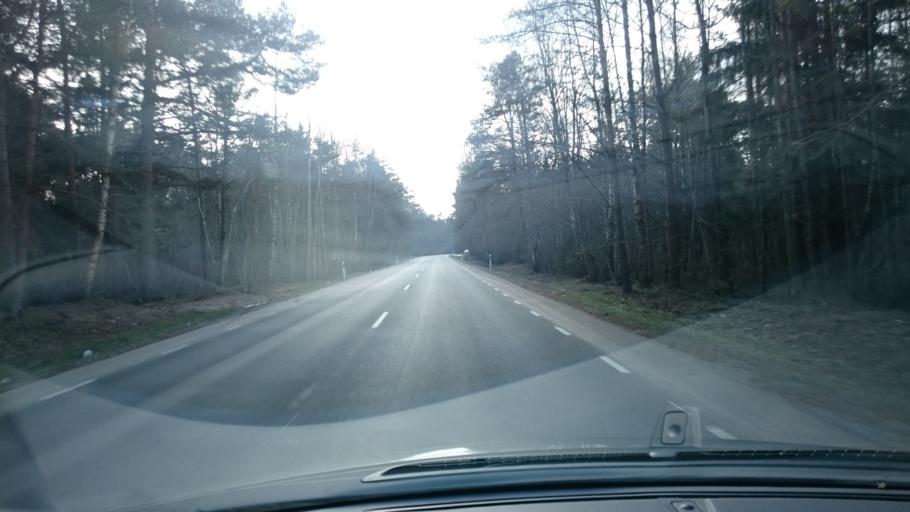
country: EE
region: Harju
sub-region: Paldiski linn
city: Paldiski
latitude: 59.3927
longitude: 24.2418
